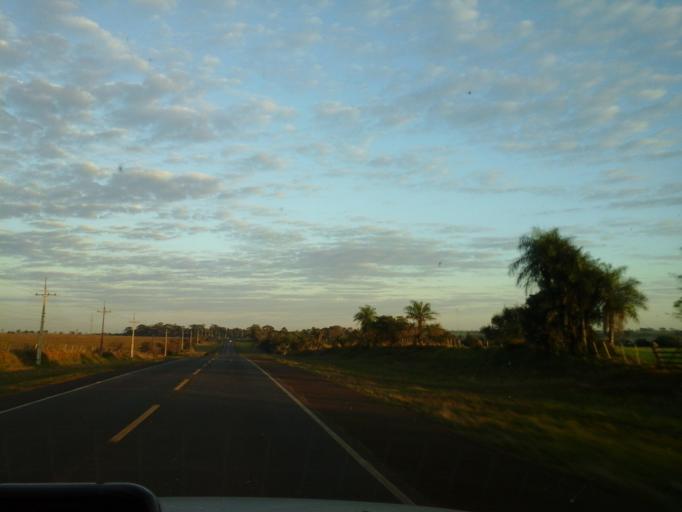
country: PY
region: Misiones
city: San Patricio
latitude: -27.0264
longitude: -56.7011
